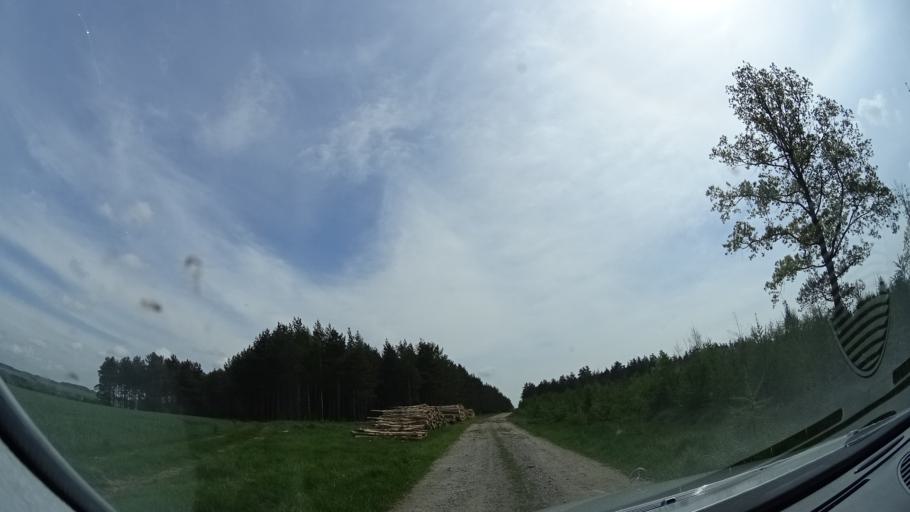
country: SE
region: Skane
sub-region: Sjobo Kommun
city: Sjoebo
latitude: 55.6725
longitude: 13.6302
